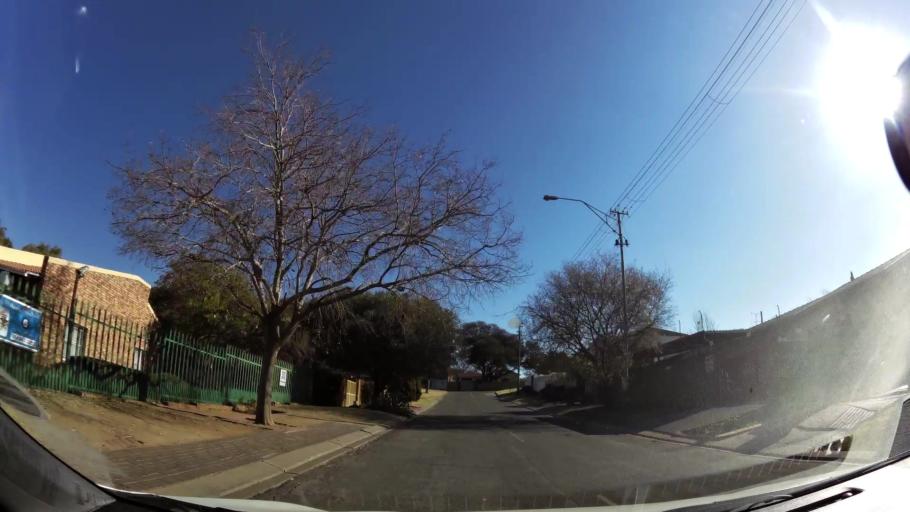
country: ZA
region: Gauteng
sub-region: City of Johannesburg Metropolitan Municipality
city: Johannesburg
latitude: -26.2787
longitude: 28.0304
